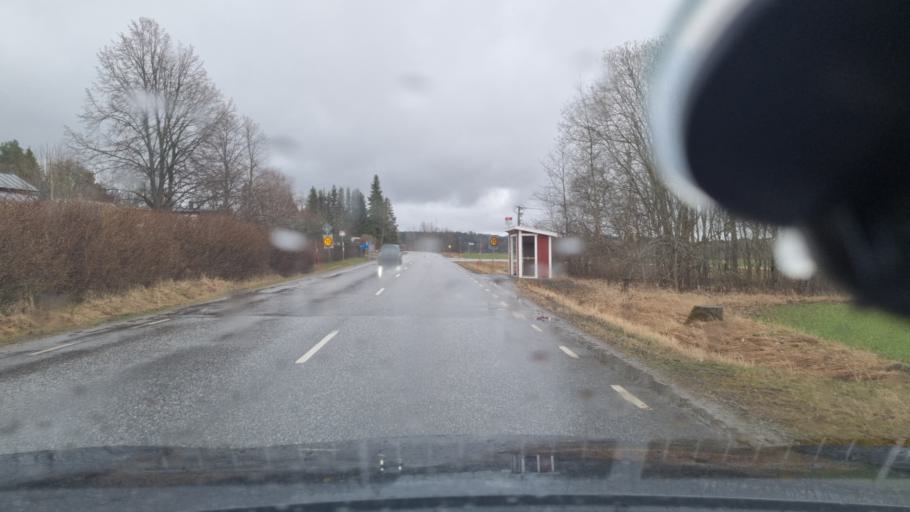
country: SE
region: Stockholm
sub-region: Sigtuna Kommun
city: Sigtuna
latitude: 59.5868
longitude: 17.6593
